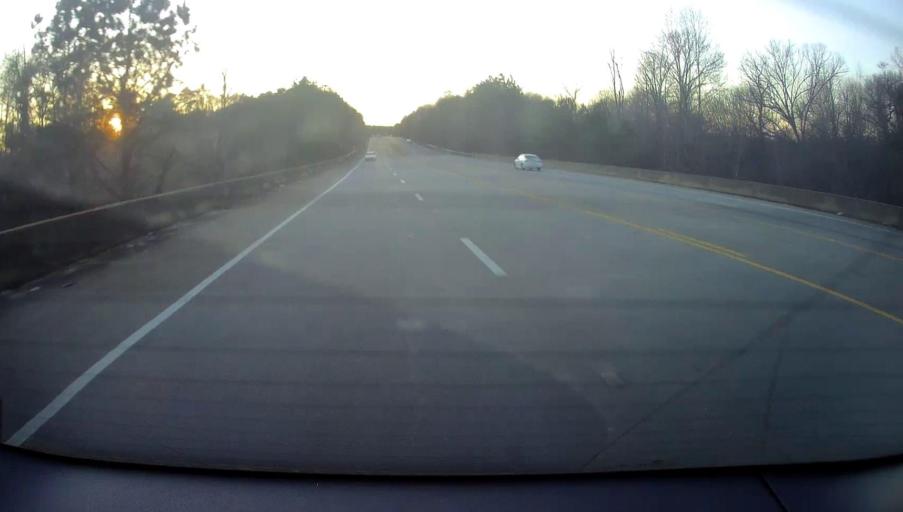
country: US
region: Georgia
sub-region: Fulton County
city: Union City
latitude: 33.5515
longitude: -84.4872
